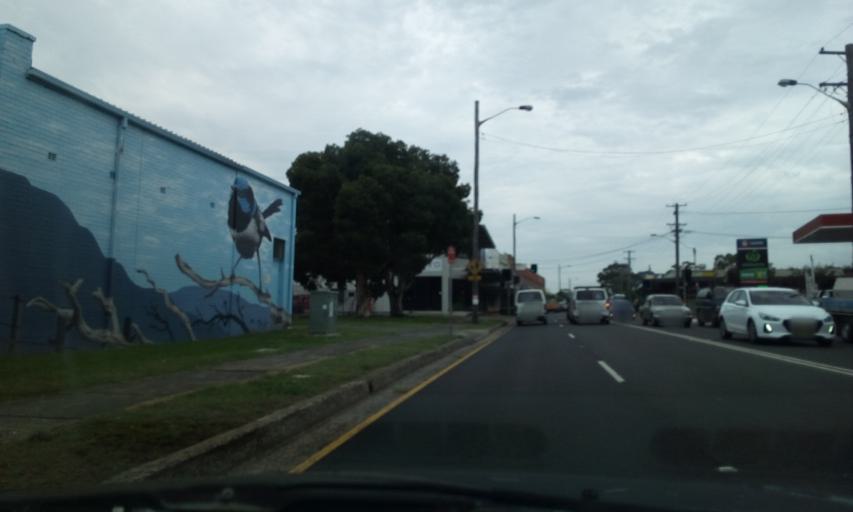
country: AU
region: New South Wales
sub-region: Wollongong
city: Cordeaux Heights
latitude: -34.4547
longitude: 150.8451
